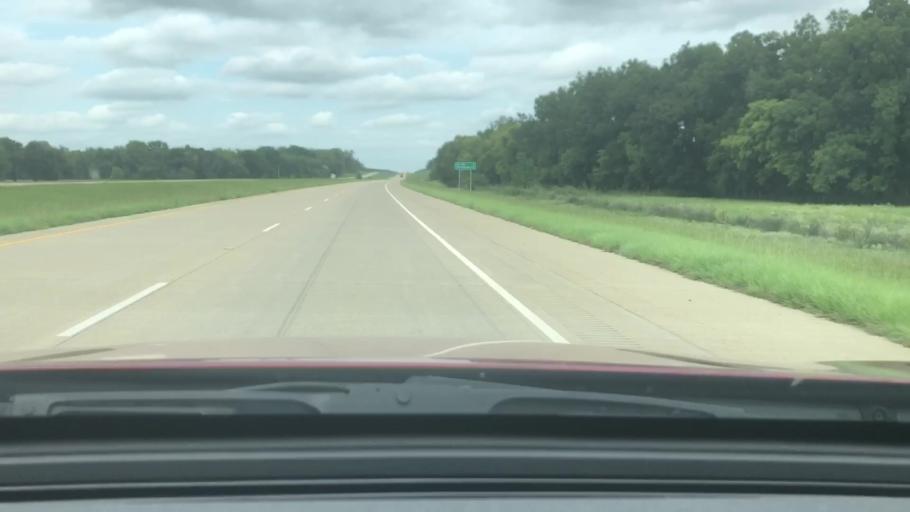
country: US
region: Louisiana
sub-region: Caddo Parish
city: Oil City
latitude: 32.7817
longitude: -93.8890
